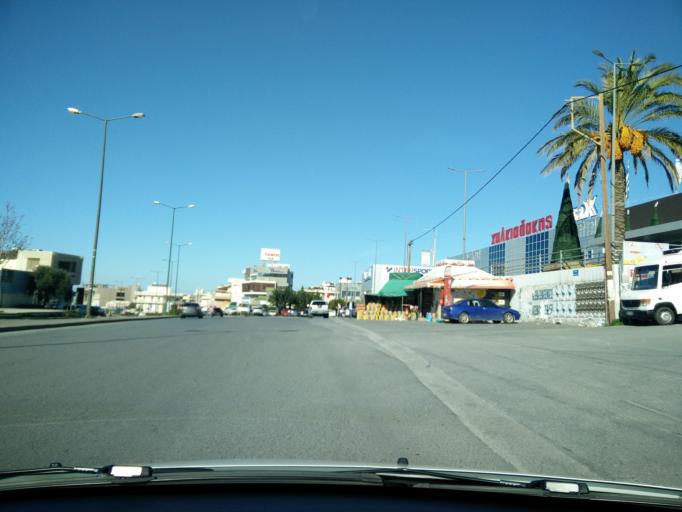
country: GR
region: Crete
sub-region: Nomos Irakleiou
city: Nea Alikarnassos
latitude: 35.3339
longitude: 25.1588
